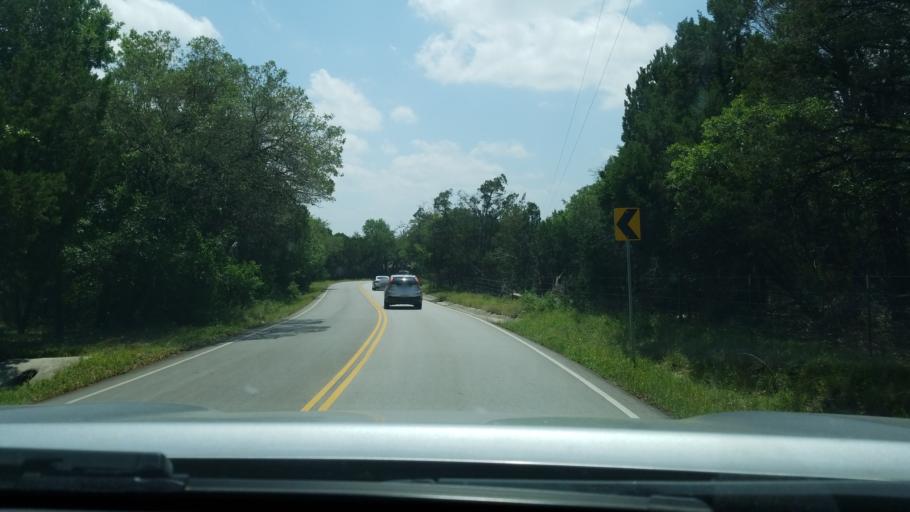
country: US
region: Texas
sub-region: Hays County
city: Woodcreek
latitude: 30.0376
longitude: -98.1156
